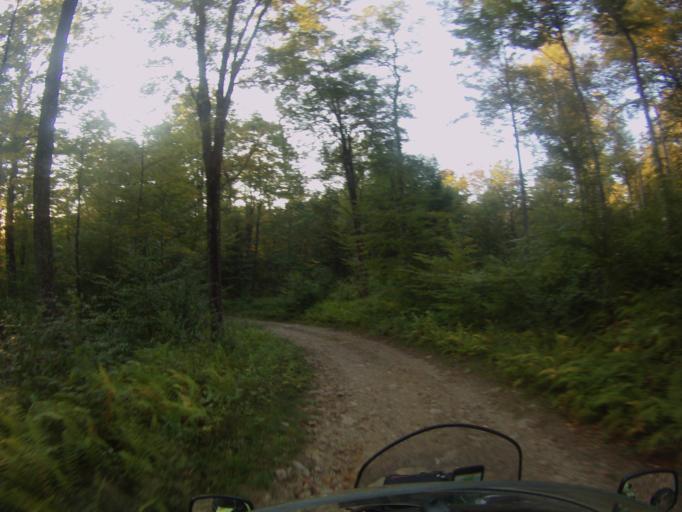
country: US
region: Vermont
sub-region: Addison County
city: Bristol
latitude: 44.0113
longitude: -73.0119
